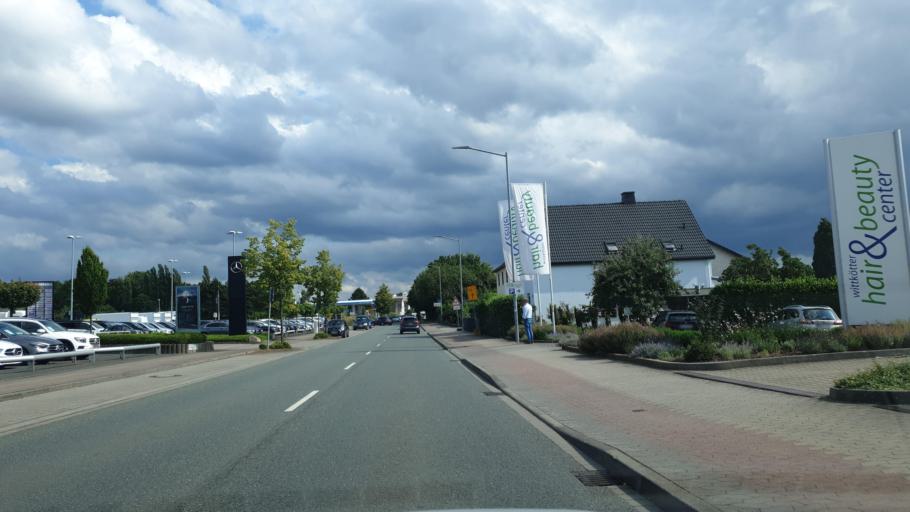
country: DE
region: North Rhine-Westphalia
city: Buende
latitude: 52.1866
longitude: 8.6019
